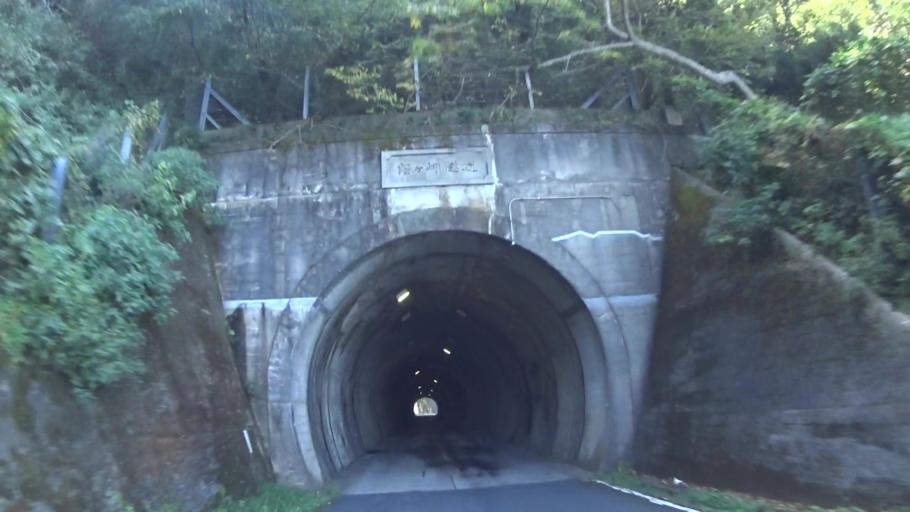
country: JP
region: Kyoto
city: Miyazu
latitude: 35.7681
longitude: 135.2312
